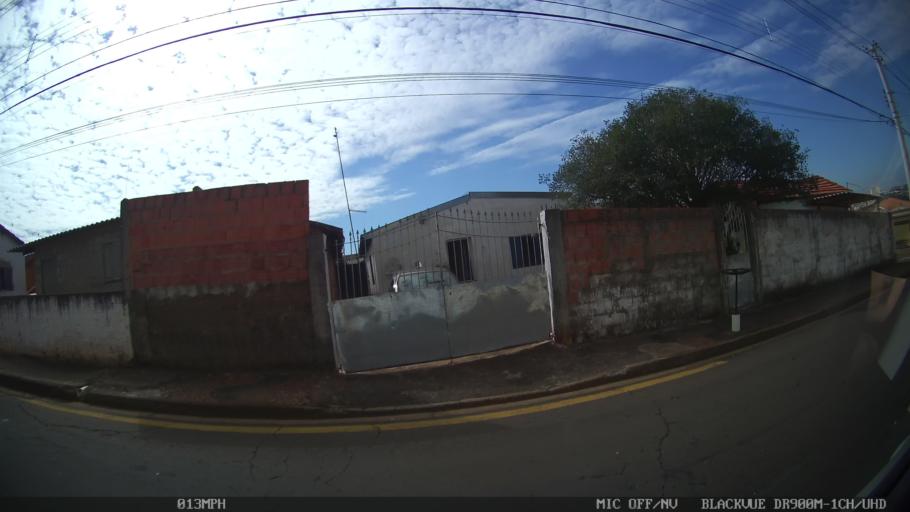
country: BR
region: Sao Paulo
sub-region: Santa Barbara D'Oeste
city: Santa Barbara d'Oeste
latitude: -22.7637
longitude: -47.4246
